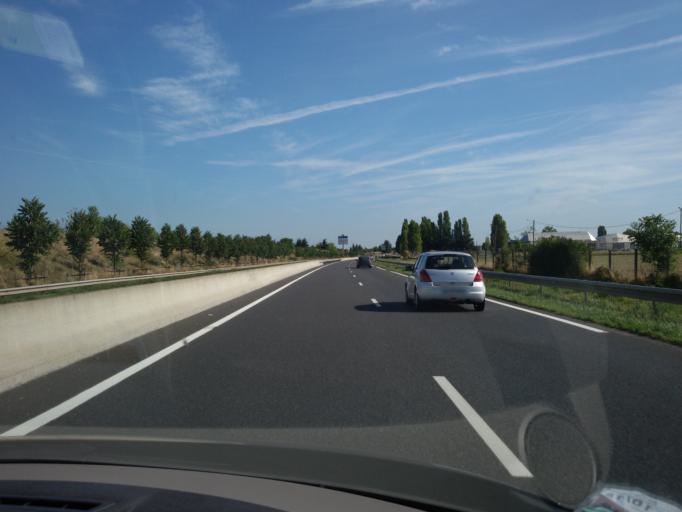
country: FR
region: Ile-de-France
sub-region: Departement de l'Essonne
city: Le Plessis-Pate
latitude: 48.5994
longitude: 2.3152
